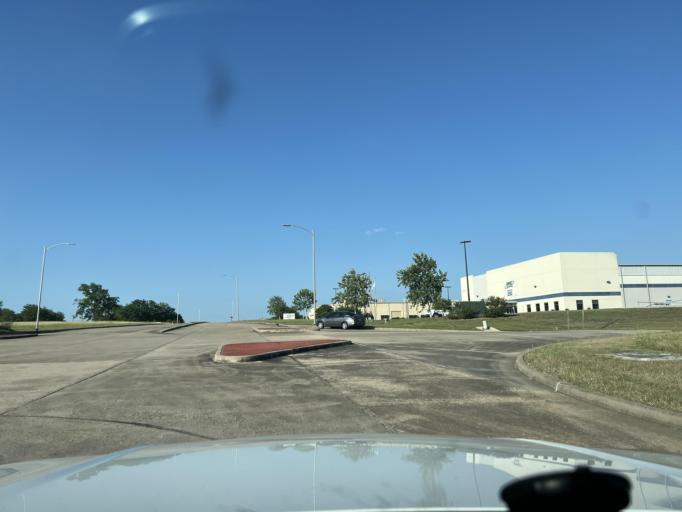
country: US
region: Texas
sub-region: Washington County
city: Brenham
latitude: 30.1373
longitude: -96.3694
